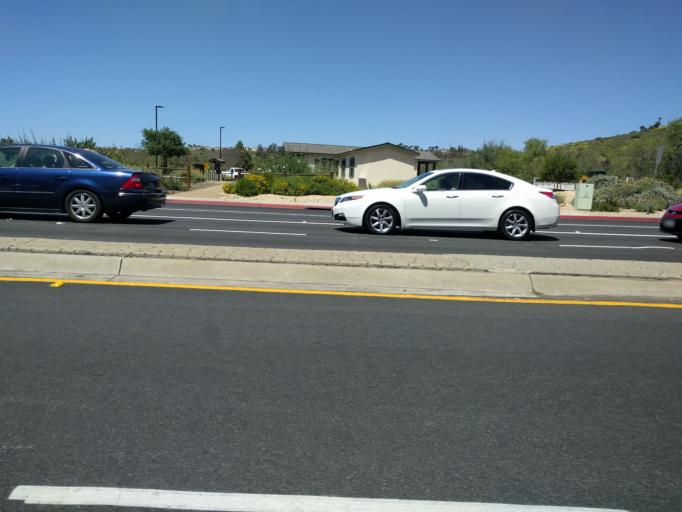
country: US
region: California
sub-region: San Diego County
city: Fairbanks Ranch
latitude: 32.9375
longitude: -117.1269
